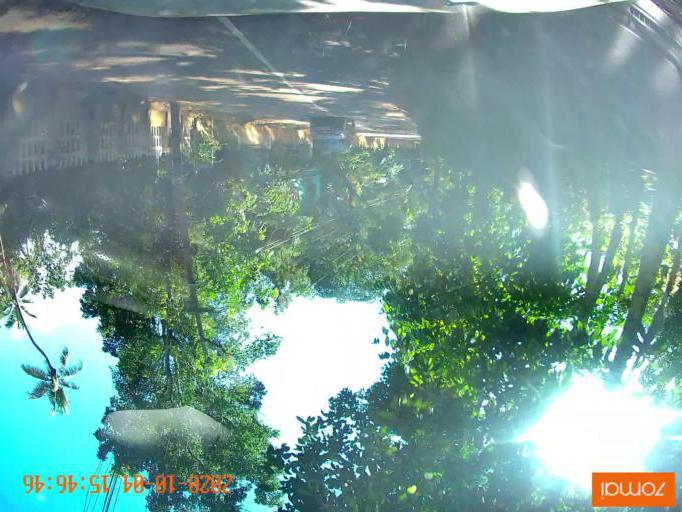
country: IN
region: Kerala
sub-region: Kottayam
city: Palackattumala
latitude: 9.7608
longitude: 76.5726
